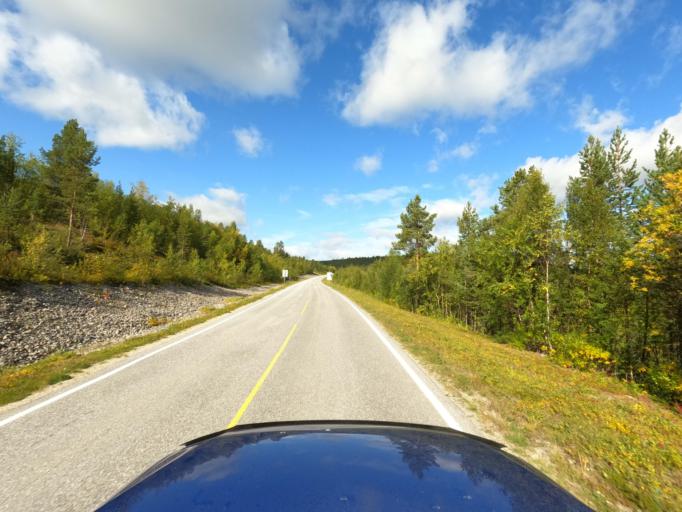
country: NO
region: Finnmark Fylke
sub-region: Karasjok
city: Karasjohka
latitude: 69.4843
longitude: 25.5098
